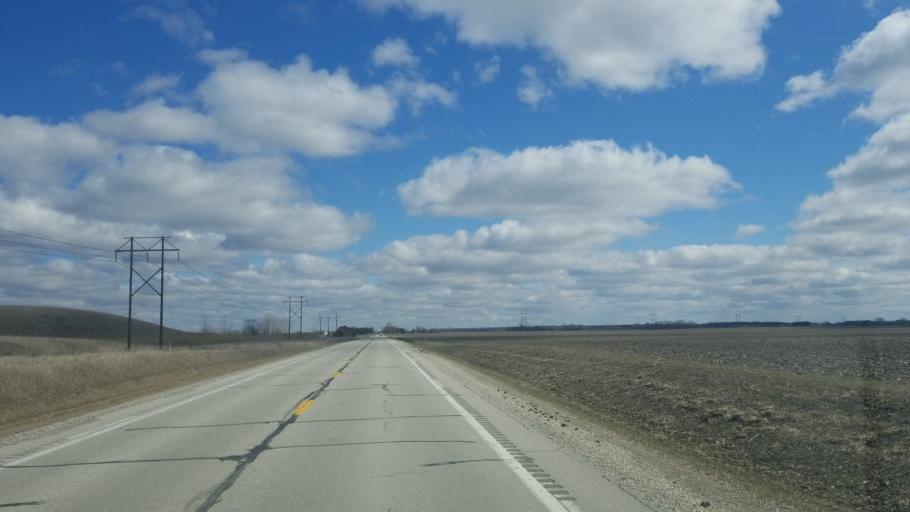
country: US
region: Illinois
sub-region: Douglas County
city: Villa Grove
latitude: 39.7921
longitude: -88.0535
